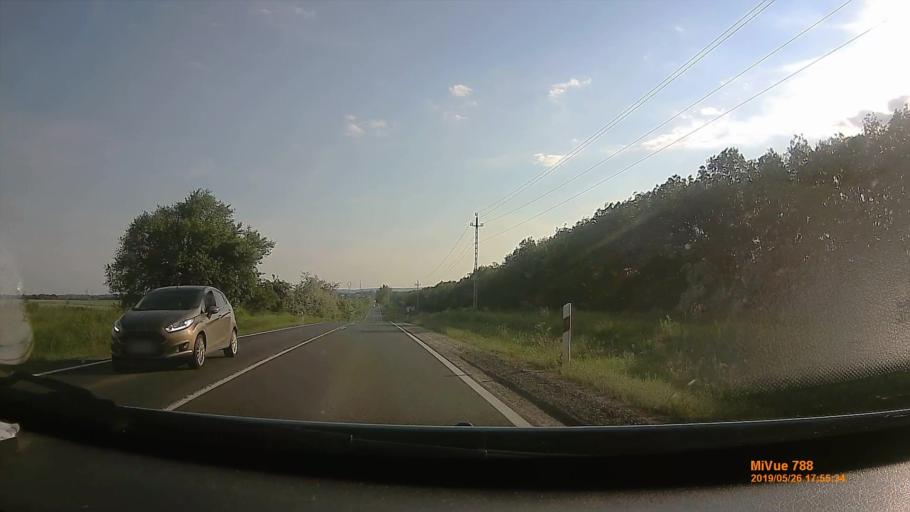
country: HU
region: Borsod-Abauj-Zemplen
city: Arnot
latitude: 48.1275
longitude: 20.8731
